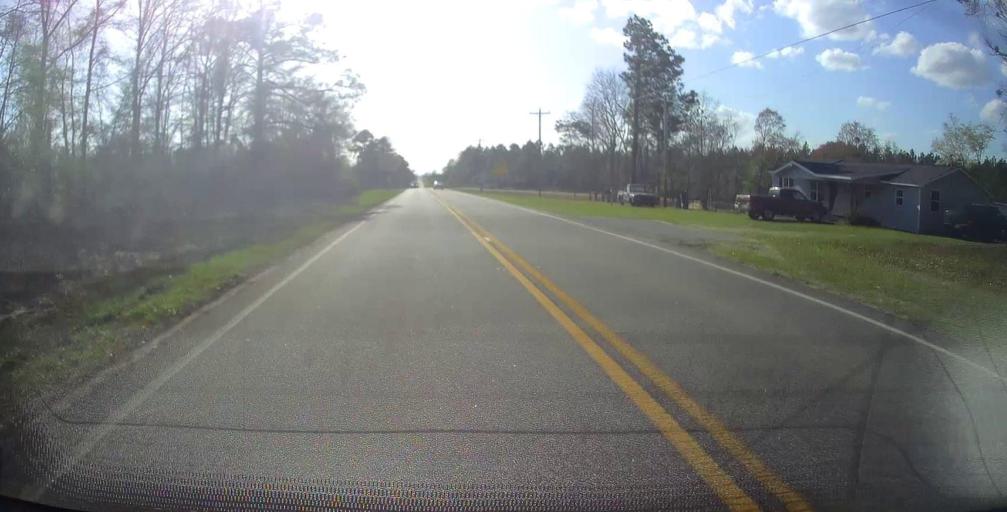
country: US
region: Georgia
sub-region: Wheeler County
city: Alamo
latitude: 32.1659
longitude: -82.7117
